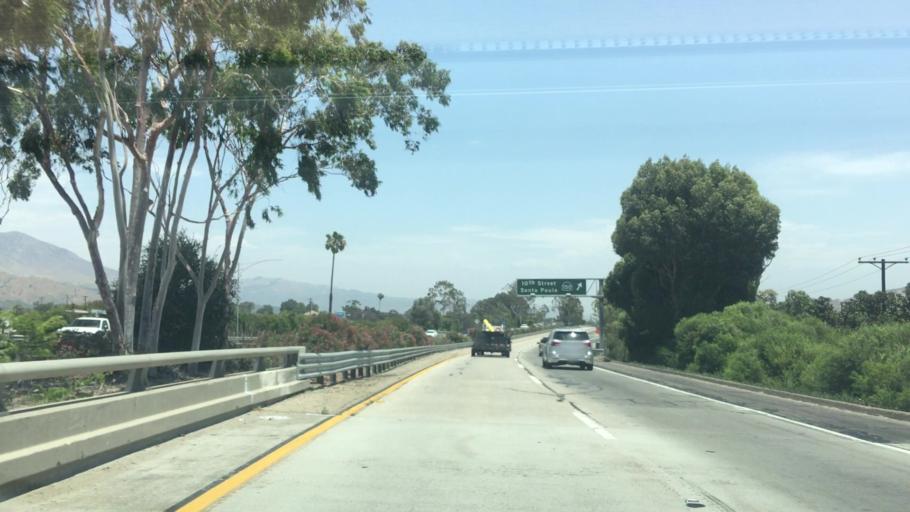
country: US
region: California
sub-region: Ventura County
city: Santa Paula
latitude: 34.3489
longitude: -119.0622
